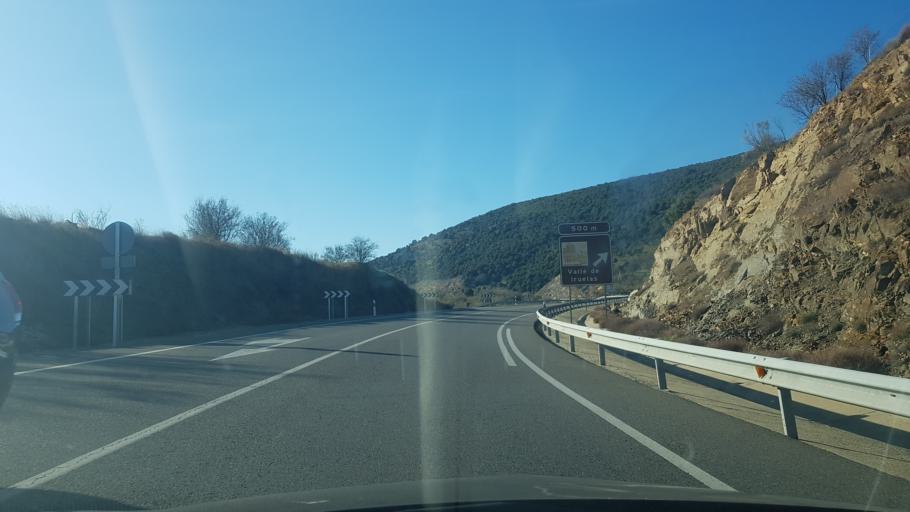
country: ES
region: Castille and Leon
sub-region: Provincia de Avila
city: El Tiemblo
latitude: 40.4301
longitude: -4.5169
